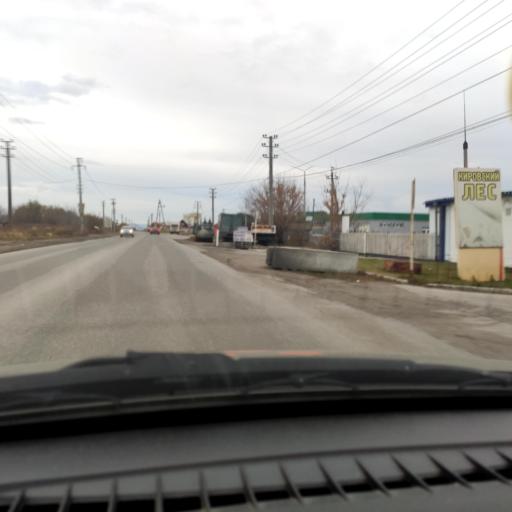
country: RU
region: Samara
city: Podstepki
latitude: 53.5229
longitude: 49.1957
